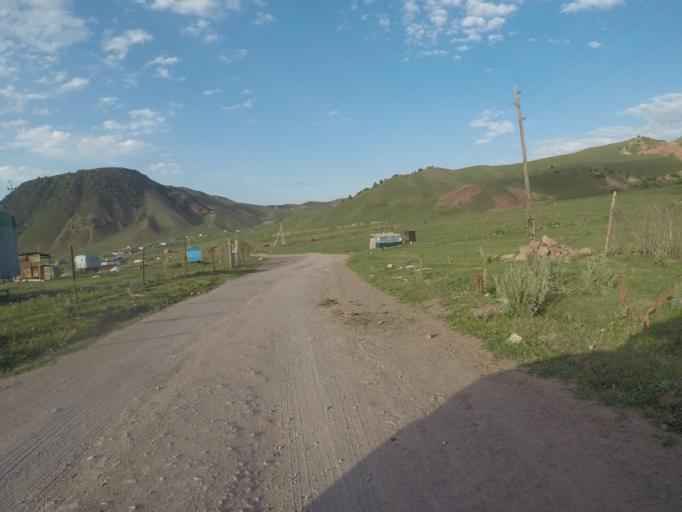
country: KG
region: Chuy
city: Bishkek
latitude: 42.6358
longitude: 74.6173
